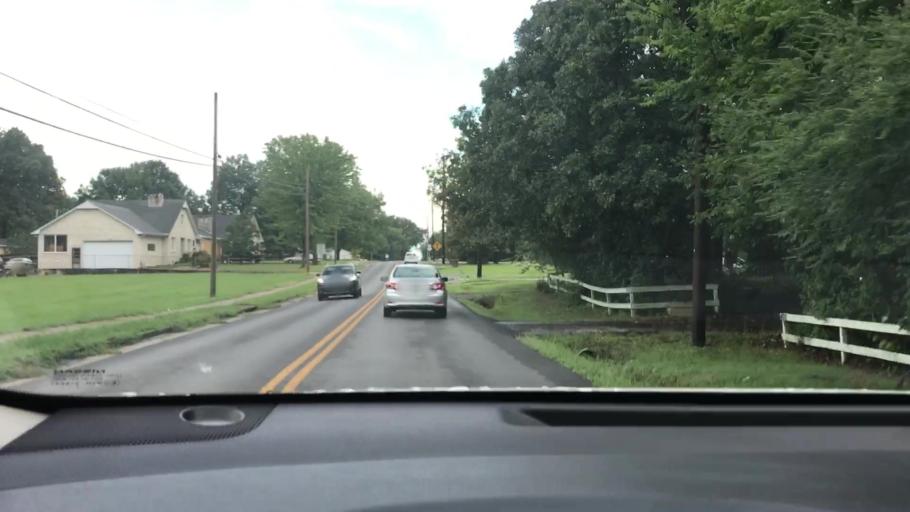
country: US
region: Kentucky
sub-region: Calloway County
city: Murray
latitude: 36.6053
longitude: -88.3245
